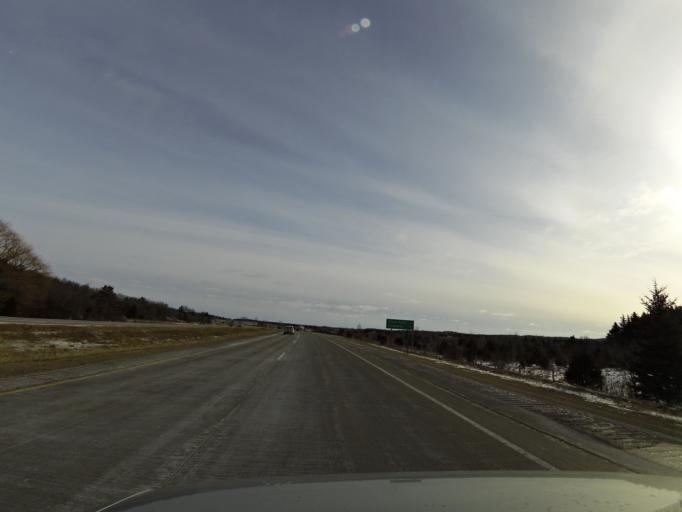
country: US
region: Wisconsin
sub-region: Saint Croix County
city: Hudson
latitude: 44.9375
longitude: -92.6921
